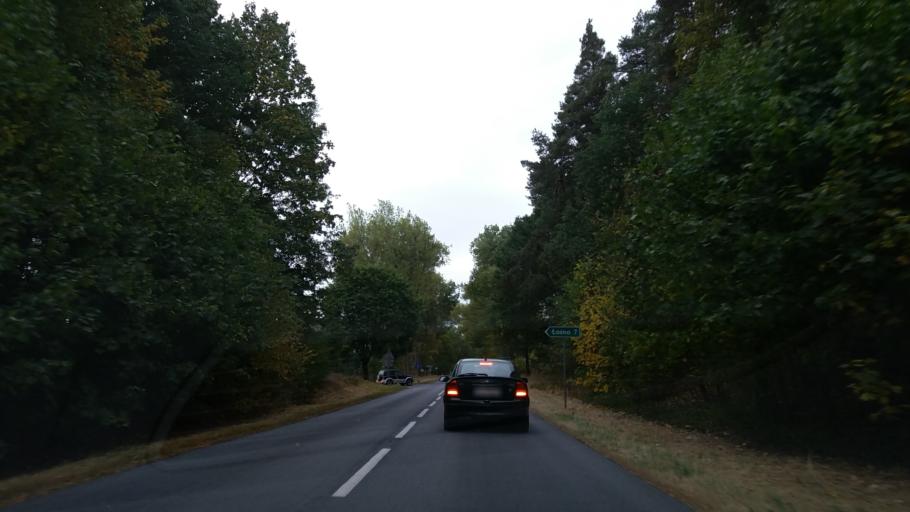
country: PL
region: Lubusz
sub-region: Powiat gorzowski
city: Klodawa
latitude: 52.8048
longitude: 15.2179
